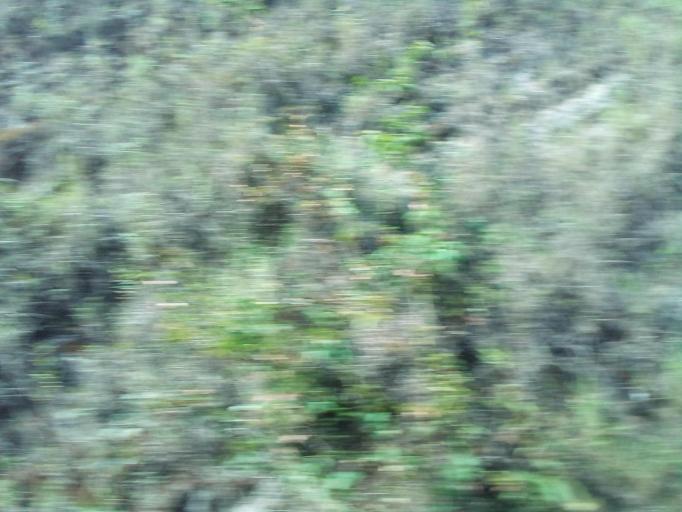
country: BR
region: Minas Gerais
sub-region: Raposos
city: Raposos
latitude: -19.8858
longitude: -43.7646
